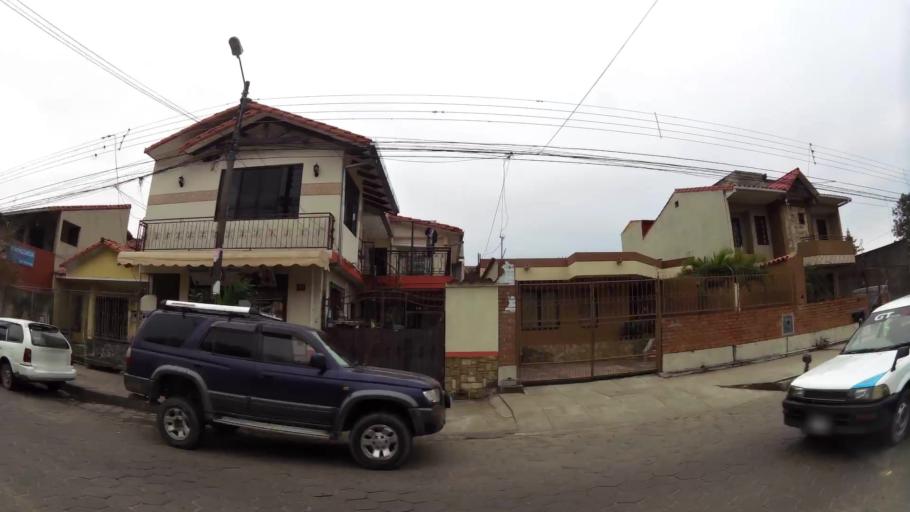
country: BO
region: Santa Cruz
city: Santa Cruz de la Sierra
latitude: -17.7985
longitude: -63.1895
